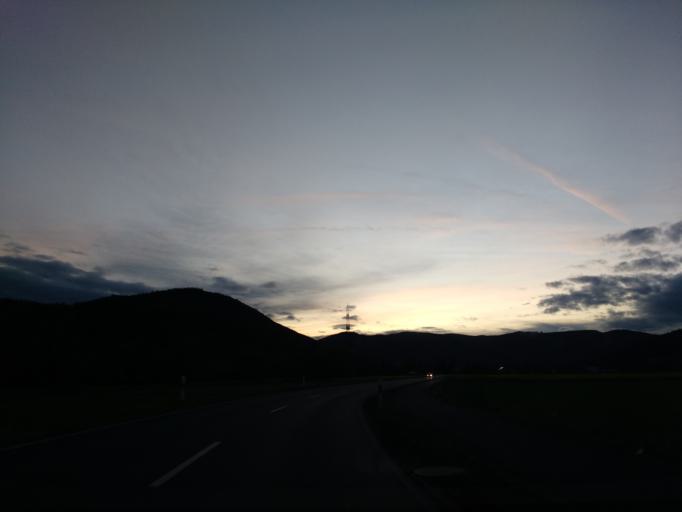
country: DE
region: Hesse
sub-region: Regierungsbezirk Kassel
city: Waldeck
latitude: 51.1694
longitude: 9.0984
